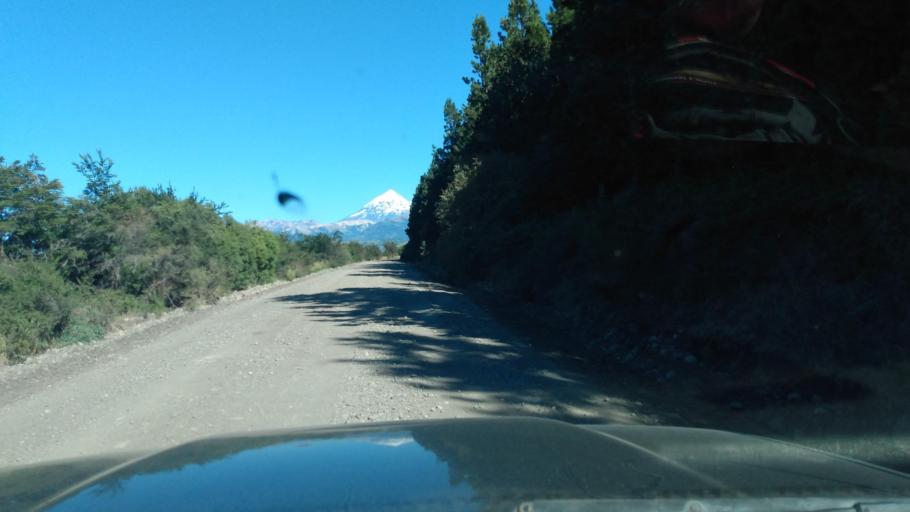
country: AR
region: Neuquen
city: Junin de los Andes
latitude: -39.7858
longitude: -71.2247
